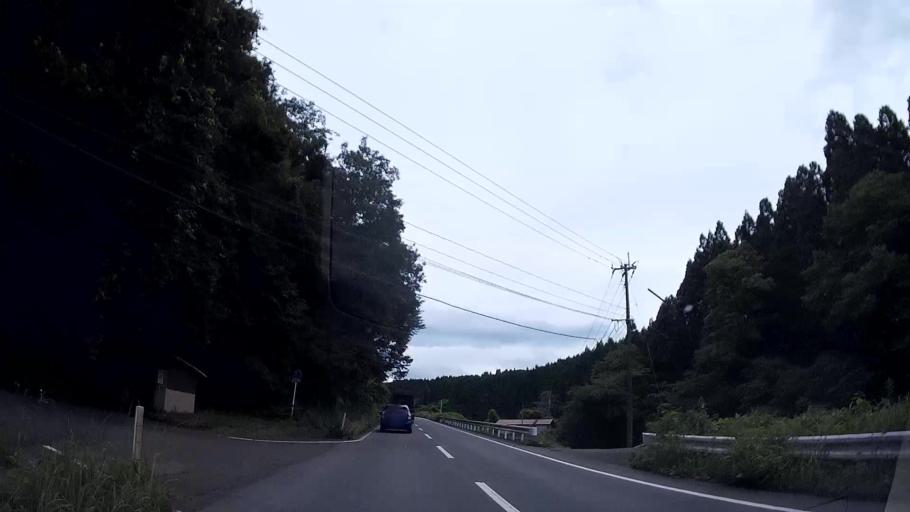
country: JP
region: Kumamoto
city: Aso
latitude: 33.1250
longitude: 131.0044
